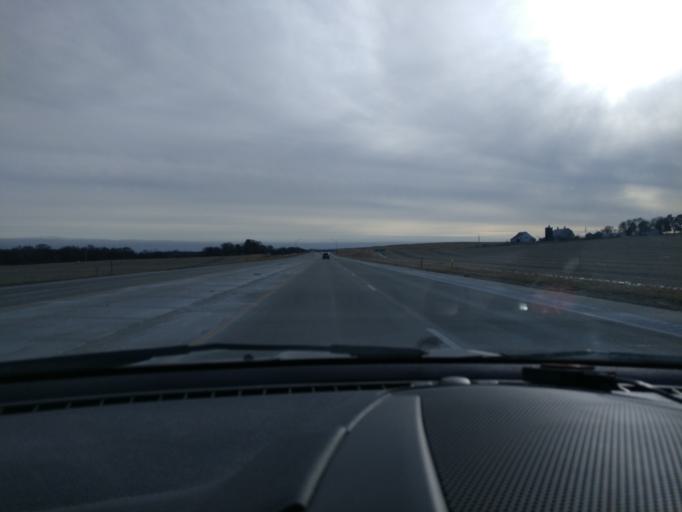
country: US
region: Nebraska
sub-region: Saunders County
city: Wahoo
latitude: 41.2234
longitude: -96.6373
